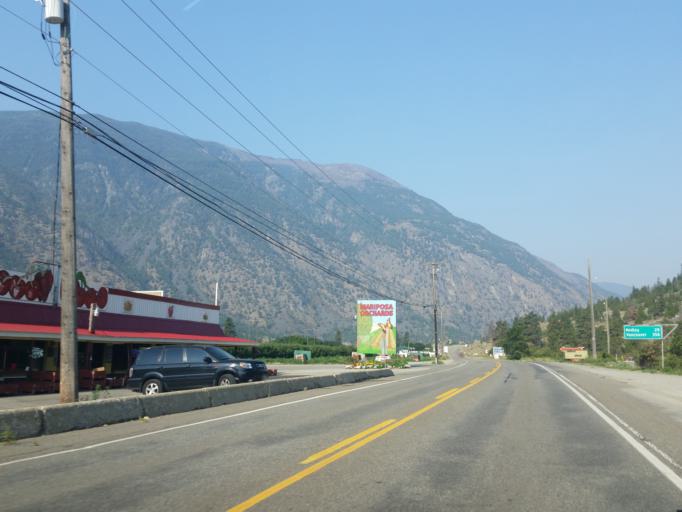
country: CA
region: British Columbia
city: Oliver
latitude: 49.2054
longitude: -119.8550
